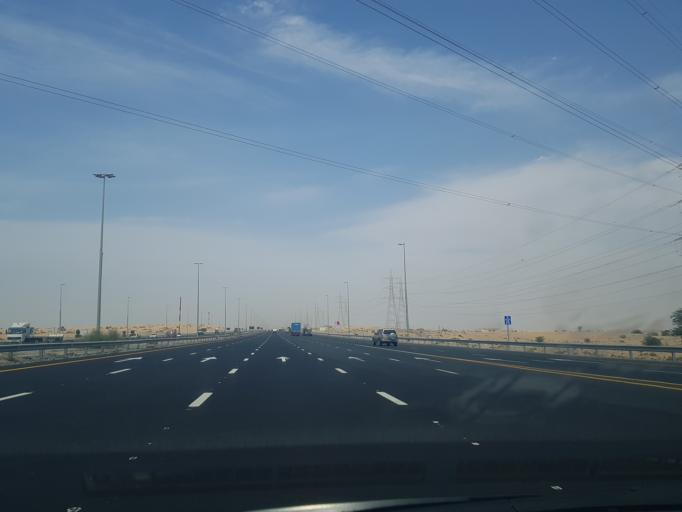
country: AE
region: Ash Shariqah
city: Sharjah
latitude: 25.2451
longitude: 55.5698
